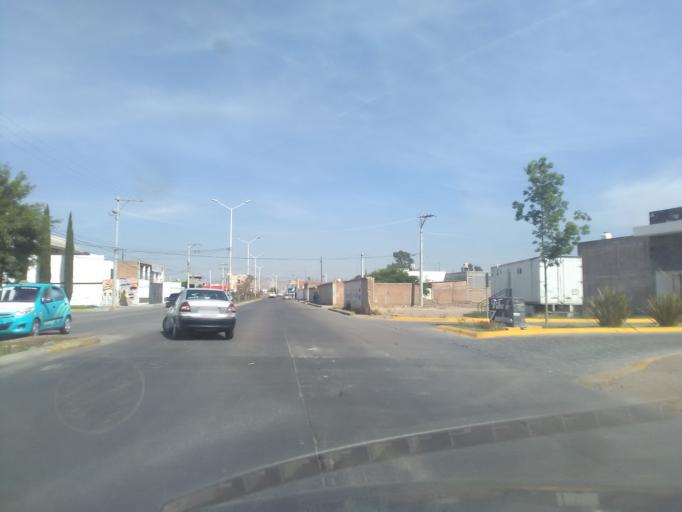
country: MX
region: Durango
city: Victoria de Durango
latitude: 24.0545
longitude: -104.6280
